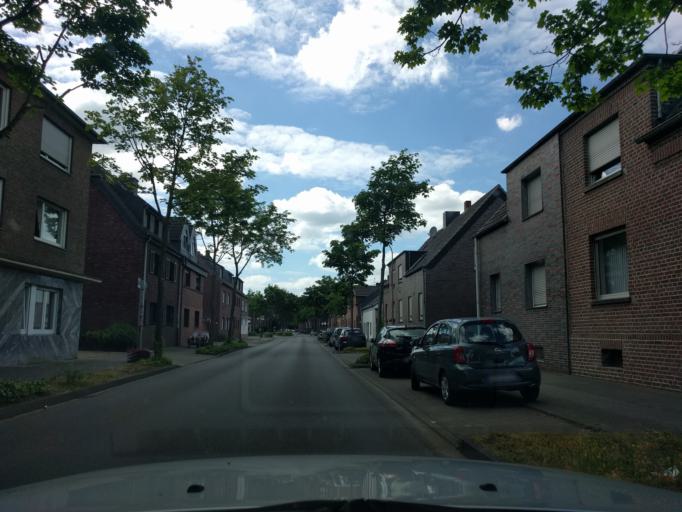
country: DE
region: North Rhine-Westphalia
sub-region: Regierungsbezirk Dusseldorf
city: Willich
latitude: 51.2438
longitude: 6.5260
